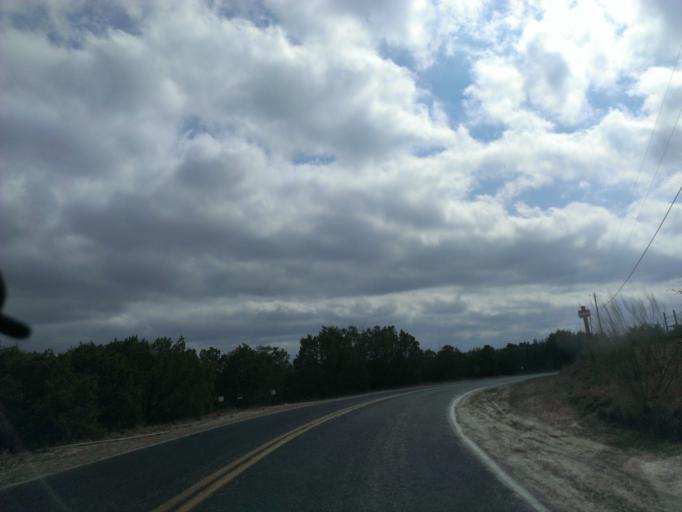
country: US
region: Texas
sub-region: Travis County
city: Briarcliff
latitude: 30.3751
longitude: -98.0924
